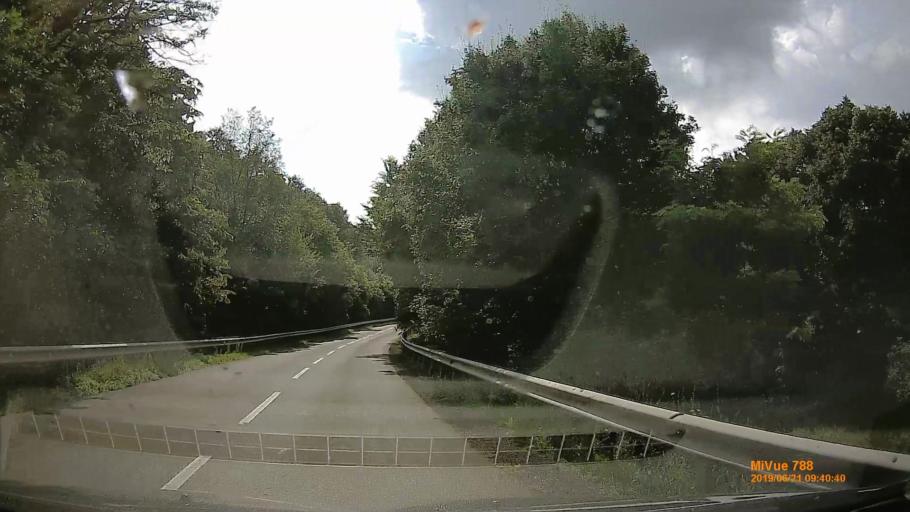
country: HU
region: Somogy
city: Taszar
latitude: 46.2949
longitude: 17.9462
